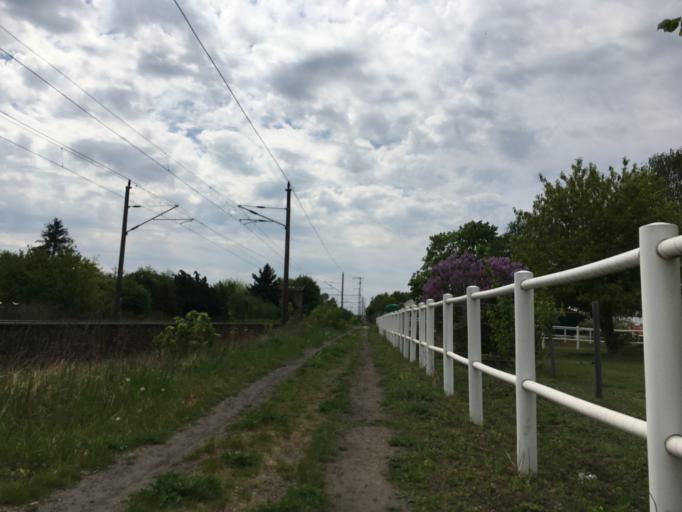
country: DE
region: Brandenburg
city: Bernau bei Berlin
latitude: 52.6868
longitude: 13.6048
